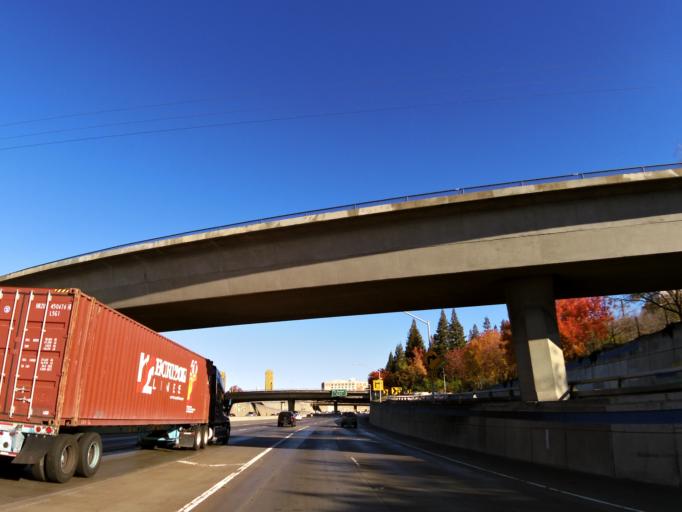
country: US
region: California
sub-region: Sacramento County
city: Sacramento
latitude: 38.5742
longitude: -121.5086
